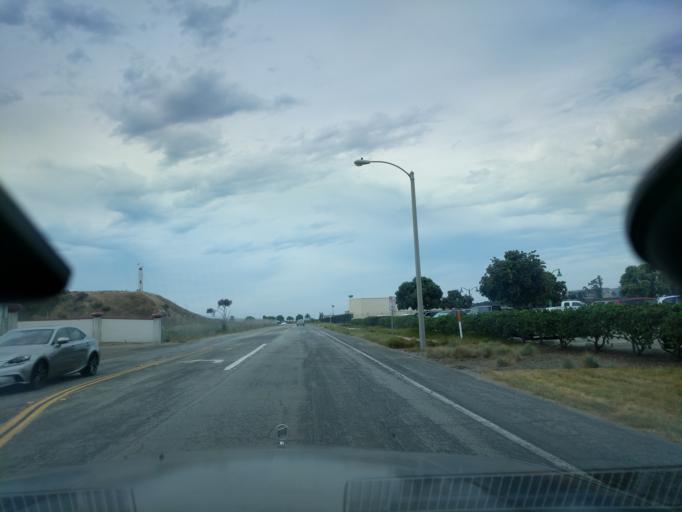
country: US
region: California
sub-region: Santa Barbara County
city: Goleta
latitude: 34.4221
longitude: -119.8353
